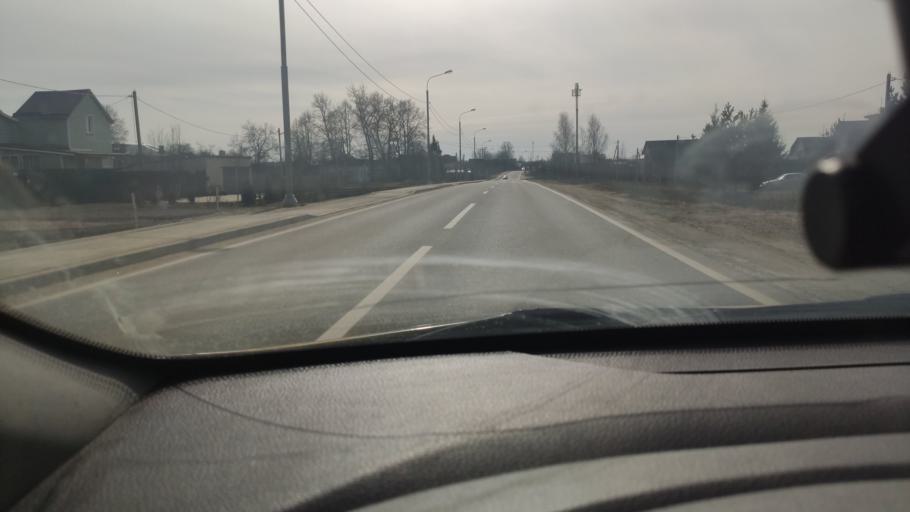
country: RU
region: Moskovskaya
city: Ruza
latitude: 55.7536
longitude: 36.1442
